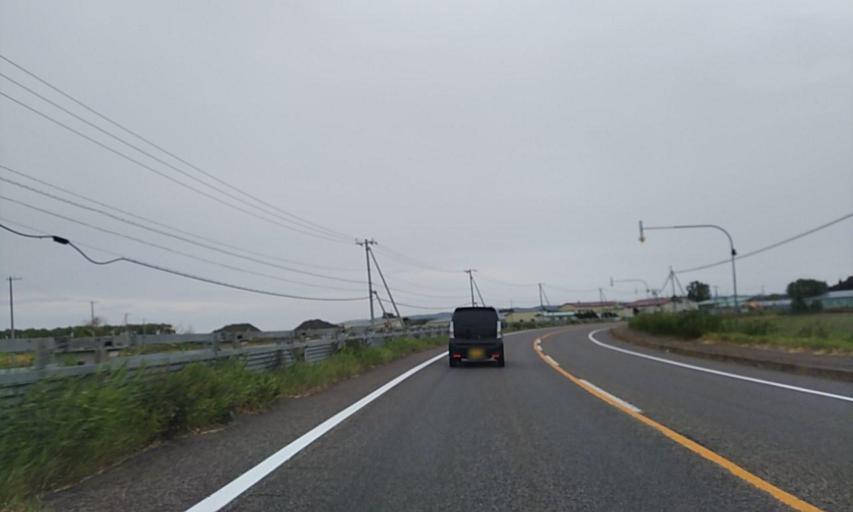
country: JP
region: Hokkaido
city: Bihoro
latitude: 43.9150
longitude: 144.1574
